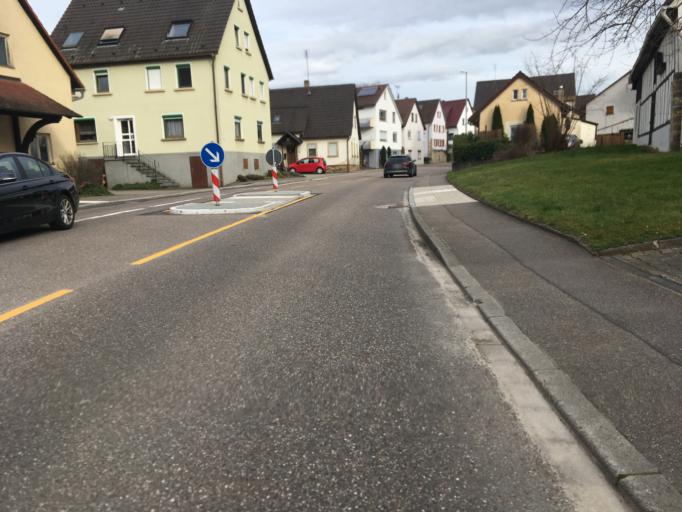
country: DE
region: Baden-Wuerttemberg
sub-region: Regierungsbezirk Stuttgart
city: Bretzfeld
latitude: 49.2143
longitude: 9.4095
